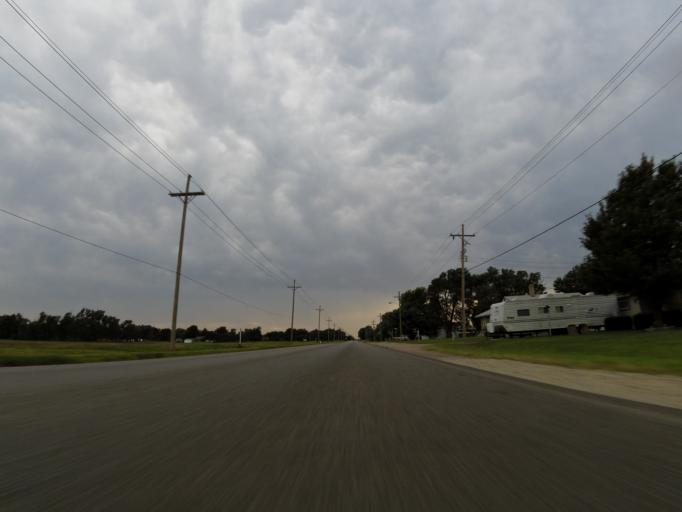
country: US
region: Kansas
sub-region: Reno County
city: South Hutchinson
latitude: 38.0283
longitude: -97.9547
